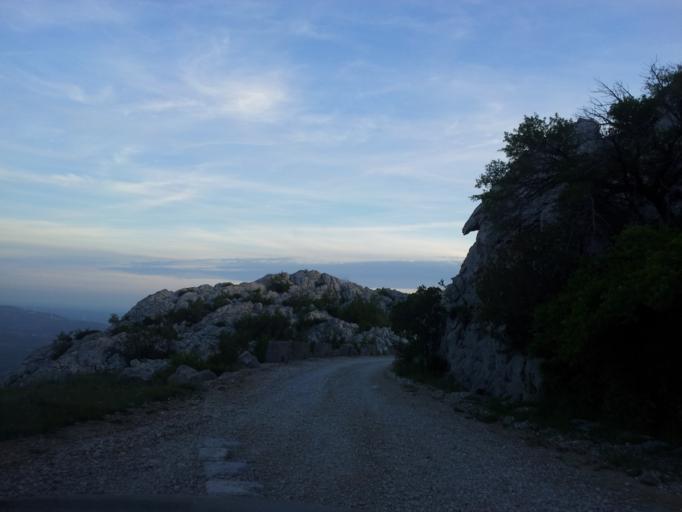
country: HR
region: Zadarska
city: Obrovac
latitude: 44.2606
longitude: 15.6412
